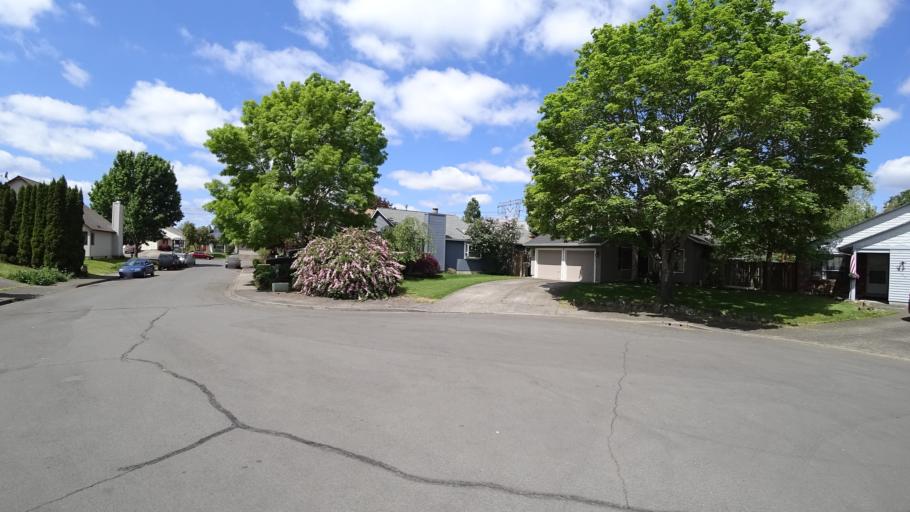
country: US
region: Oregon
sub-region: Washington County
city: Aloha
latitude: 45.5094
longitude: -122.8953
